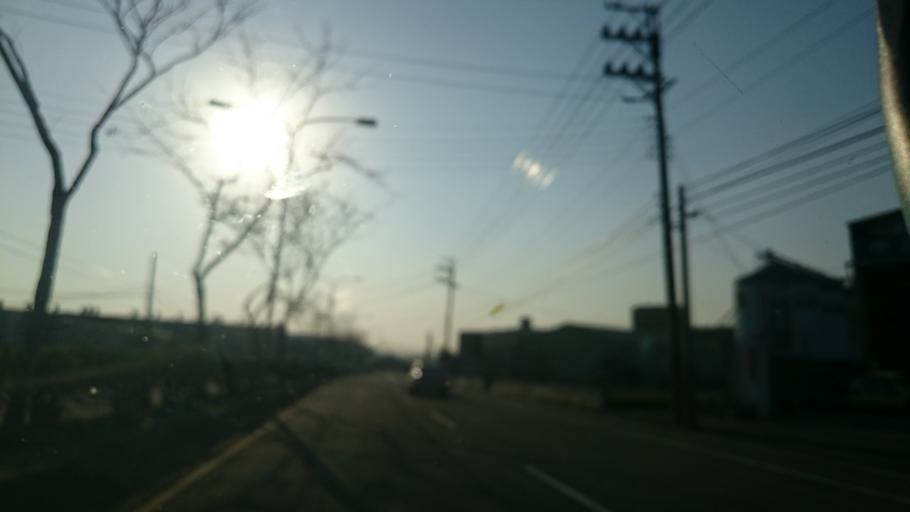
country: TW
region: Taiwan
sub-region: Miaoli
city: Miaoli
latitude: 24.6219
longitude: 120.8109
